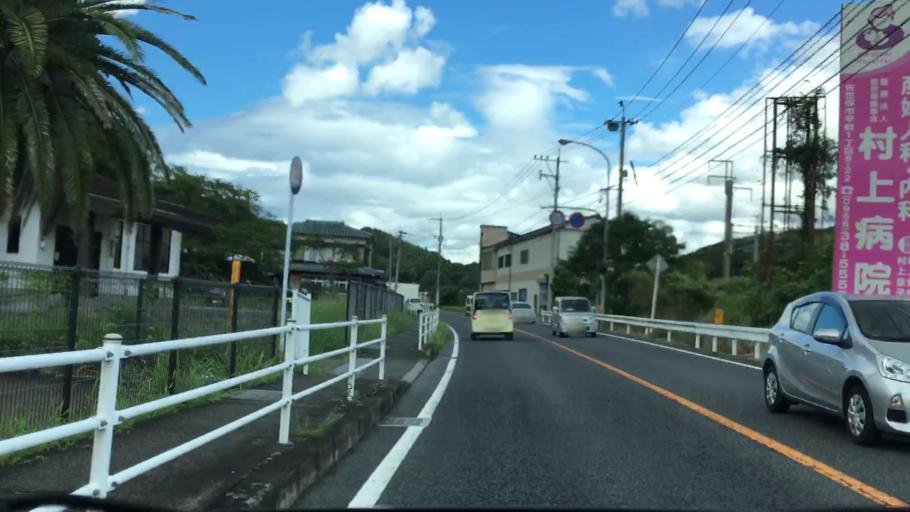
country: JP
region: Nagasaki
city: Sasebo
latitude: 33.1543
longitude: 129.8304
